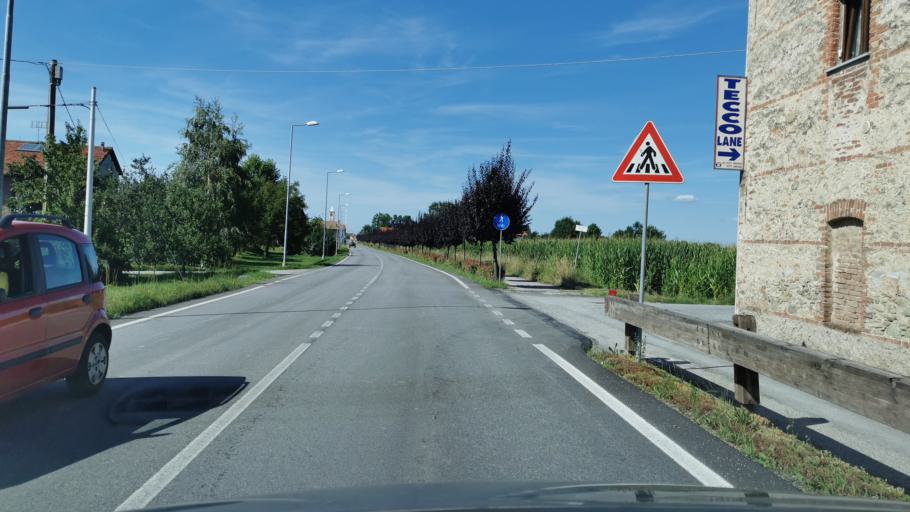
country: IT
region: Piedmont
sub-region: Provincia di Cuneo
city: Boves
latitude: 44.3389
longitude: 7.5572
